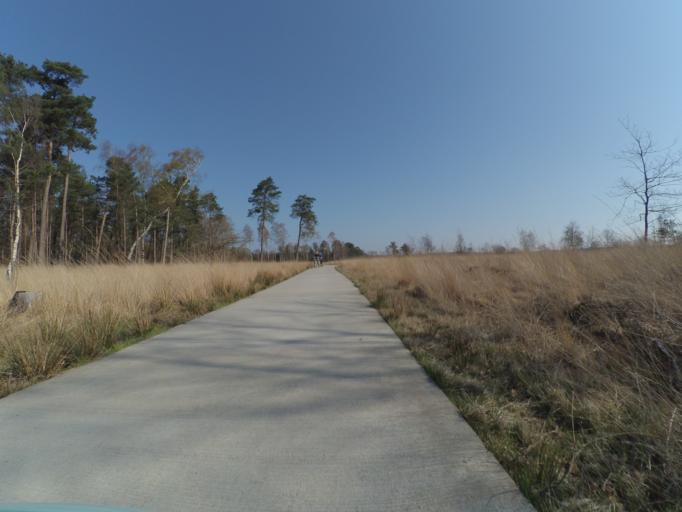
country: NL
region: Gelderland
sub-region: Gemeente Ede
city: Otterlo
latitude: 52.0946
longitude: 5.8554
